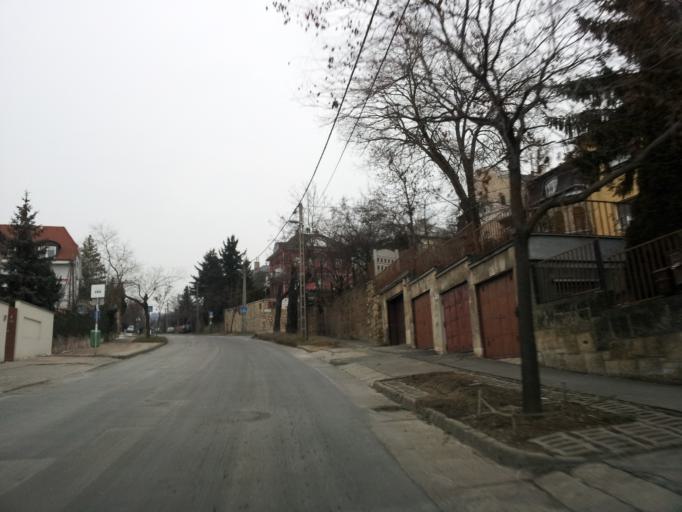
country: HU
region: Budapest
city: Budapest XII. keruelet
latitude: 47.4792
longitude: 19.0014
